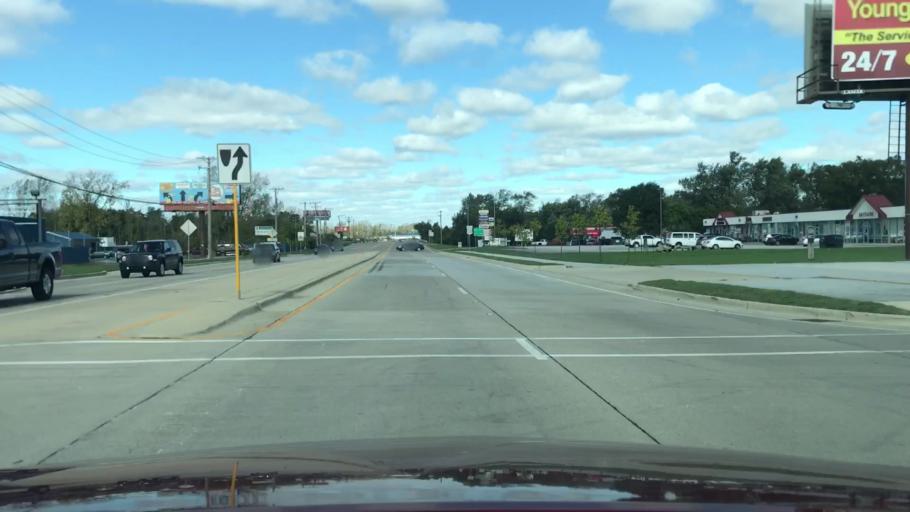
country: US
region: Indiana
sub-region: Lake County
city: Dyer
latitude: 41.5019
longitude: -87.5298
